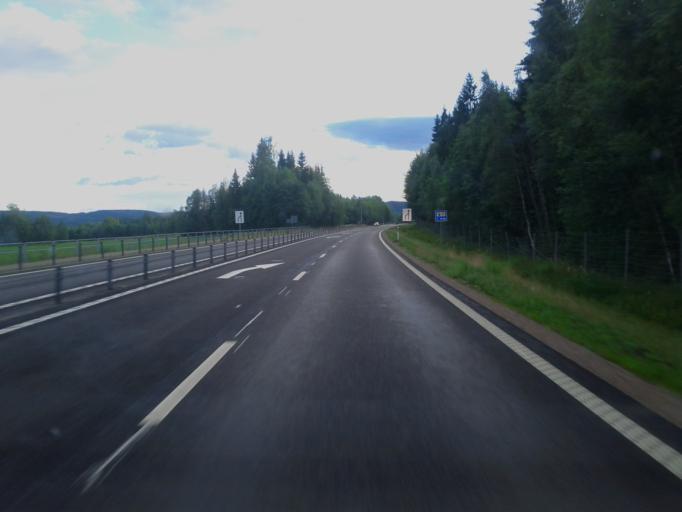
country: SE
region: Dalarna
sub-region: Borlange Kommun
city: Borlaenge
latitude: 60.4382
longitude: 15.3561
